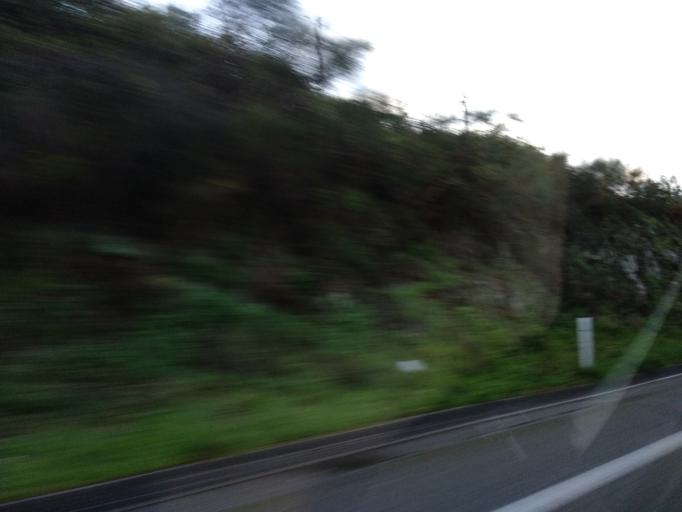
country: PT
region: Braga
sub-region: Braga
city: Oliveira
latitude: 41.4900
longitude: -8.4656
